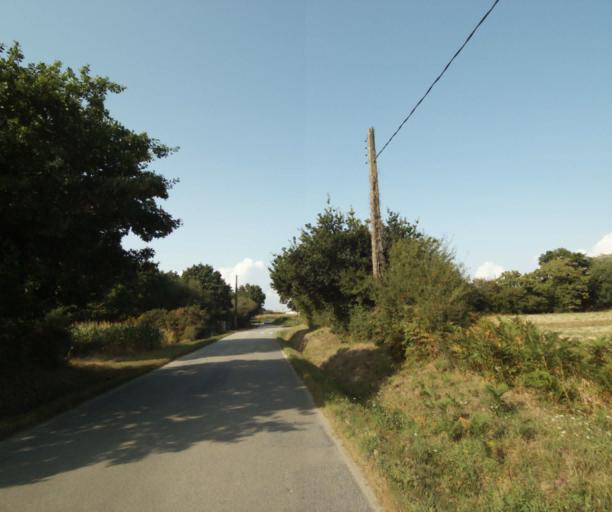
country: FR
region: Brittany
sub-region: Departement du Morbihan
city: Riantec
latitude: 47.7241
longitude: -3.2962
